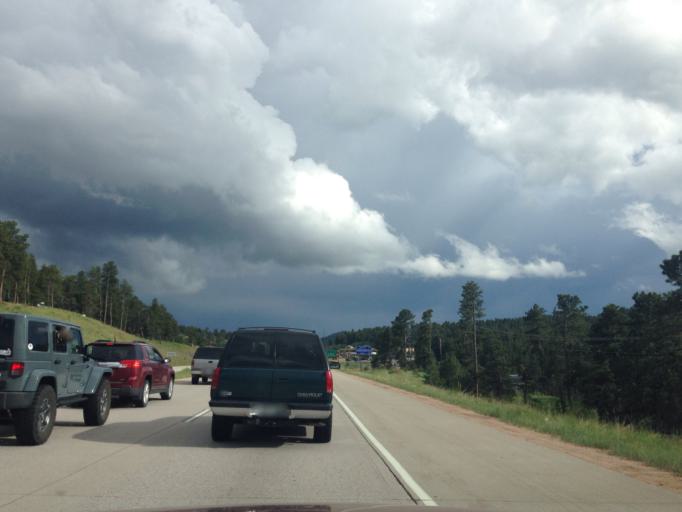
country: US
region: Colorado
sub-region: Jefferson County
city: Evergreen
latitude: 39.5249
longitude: -105.3070
